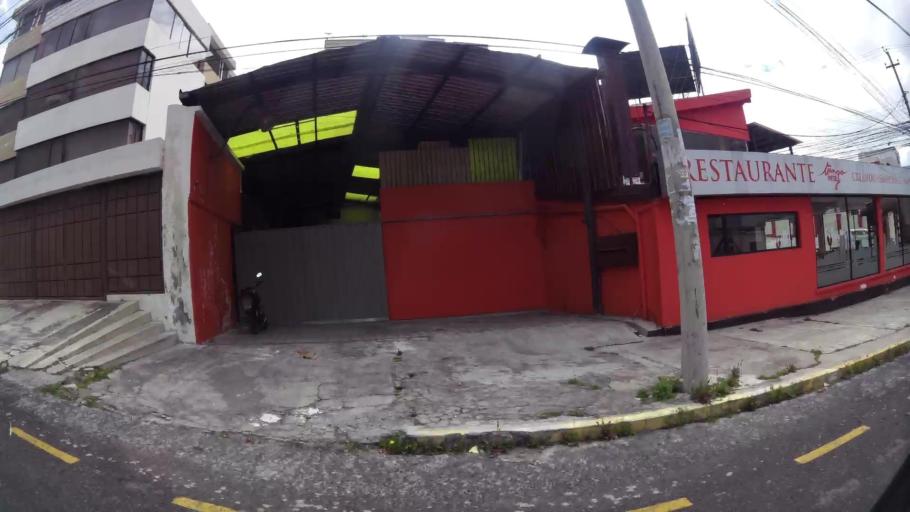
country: EC
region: Pichincha
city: Quito
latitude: -0.1660
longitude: -78.4878
